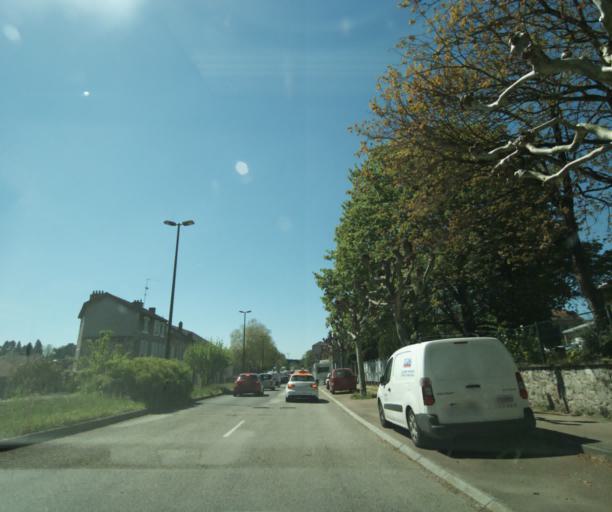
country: FR
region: Limousin
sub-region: Departement de la Haute-Vienne
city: Limoges
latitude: 45.8227
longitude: 1.2654
